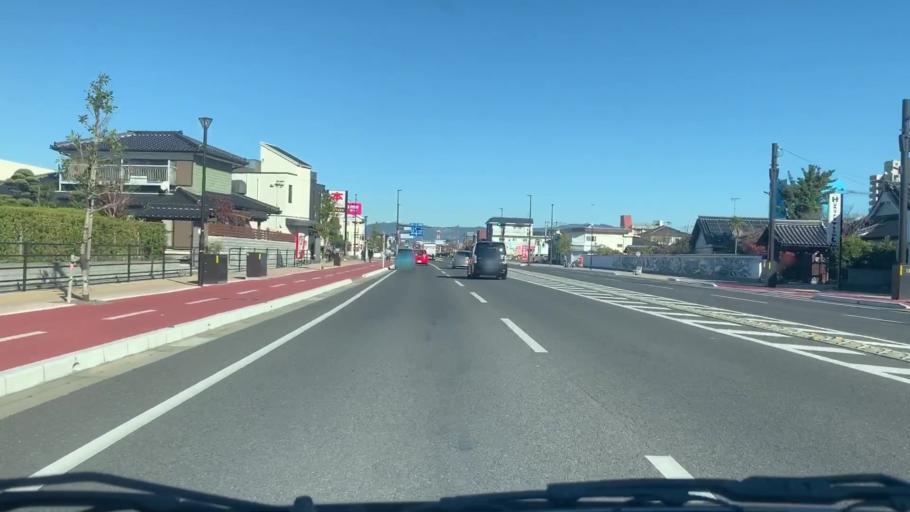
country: JP
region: Saga Prefecture
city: Saga-shi
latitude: 33.2475
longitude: 130.2929
